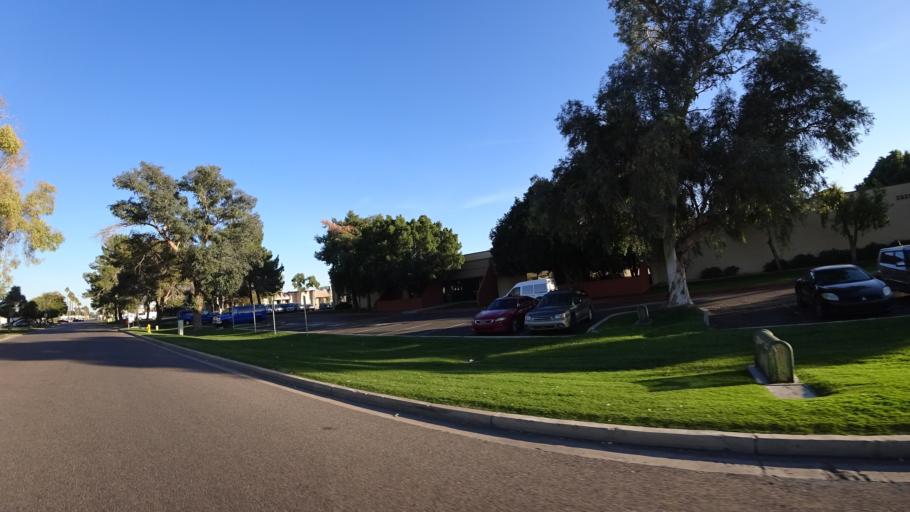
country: US
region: Arizona
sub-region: Maricopa County
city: Phoenix
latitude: 33.4224
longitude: -112.0329
